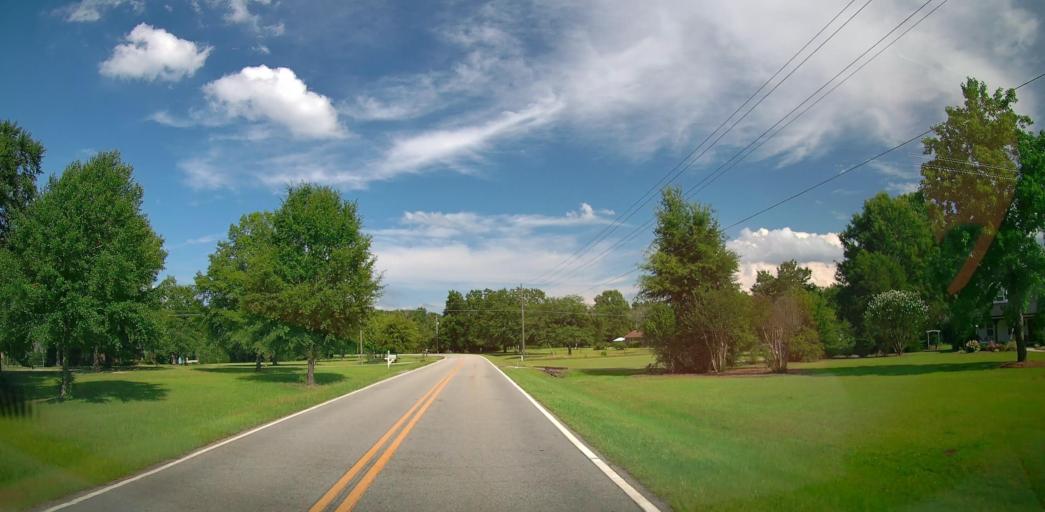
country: US
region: Georgia
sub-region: Houston County
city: Robins Air Force Base
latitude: 32.5329
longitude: -83.6394
